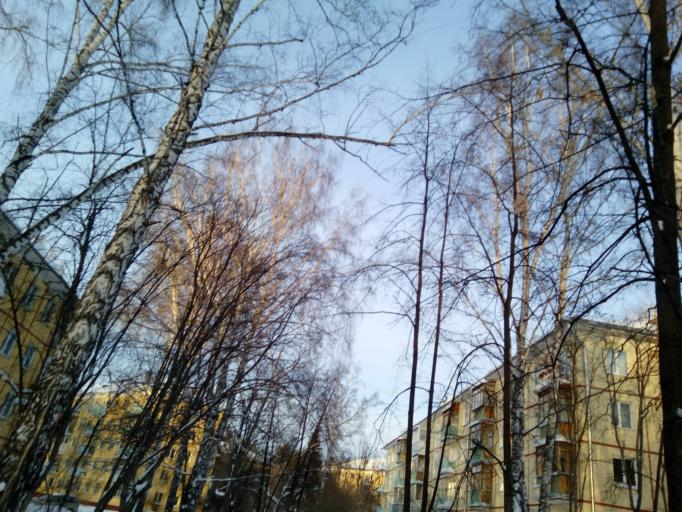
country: RU
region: Novosibirsk
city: Akademgorodok
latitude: 54.8386
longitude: 83.1098
